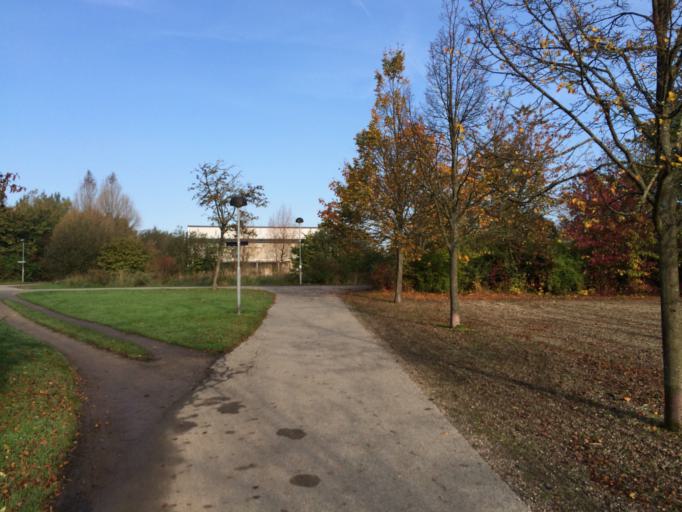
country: SE
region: Skane
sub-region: Lunds Kommun
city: Lund
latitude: 55.7088
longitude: 13.2407
